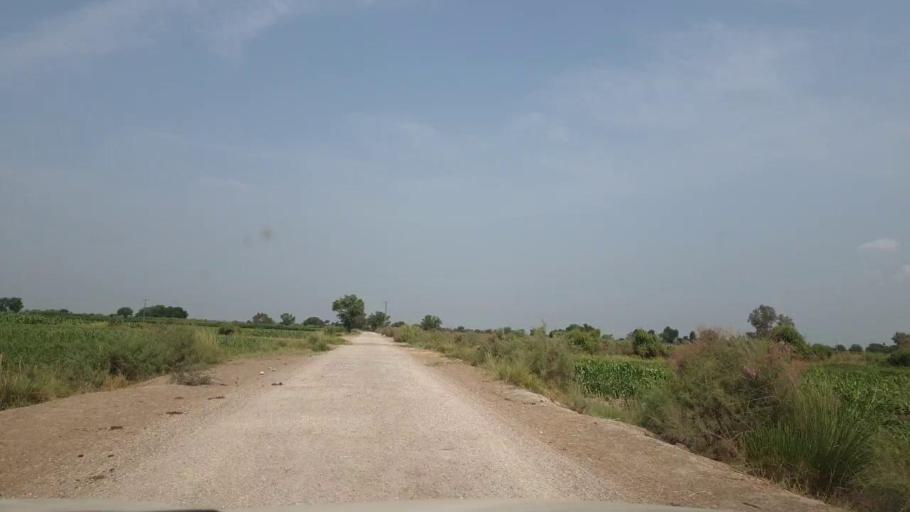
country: PK
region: Sindh
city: Sobhadero
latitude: 27.3889
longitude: 68.2720
